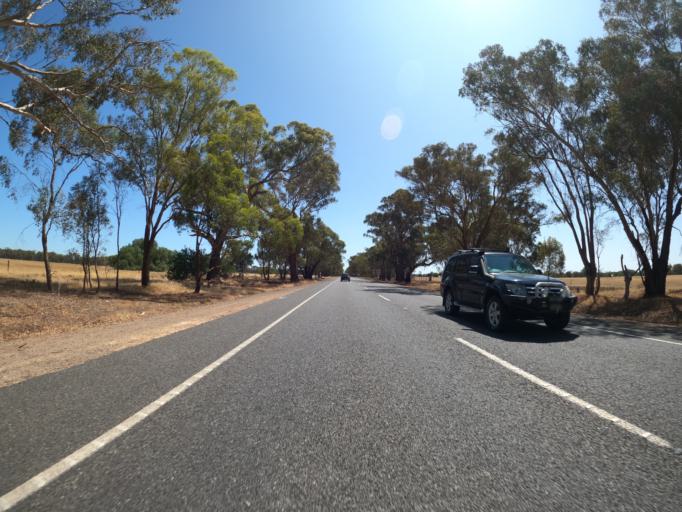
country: AU
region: New South Wales
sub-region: Corowa Shire
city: Corowa
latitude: -36.0616
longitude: 146.4078
